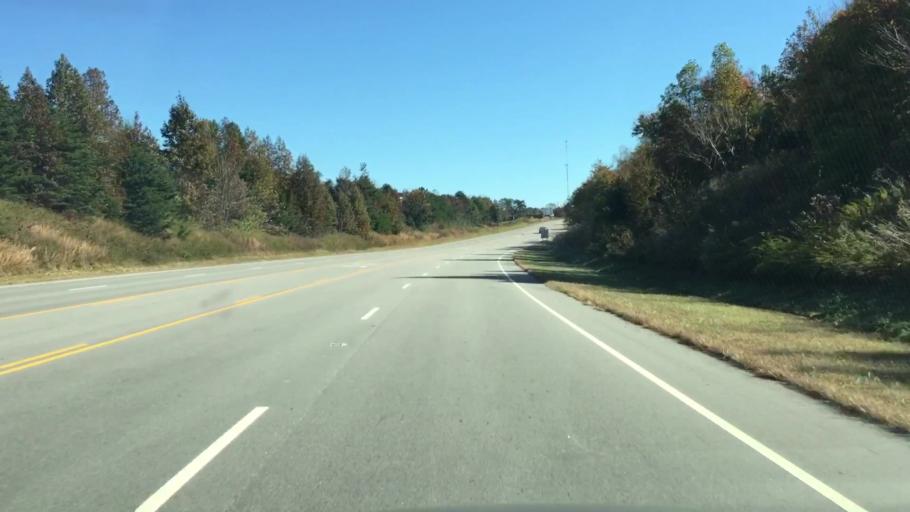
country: US
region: North Carolina
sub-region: Rockingham County
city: Reidsville
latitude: 36.3124
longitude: -79.6386
